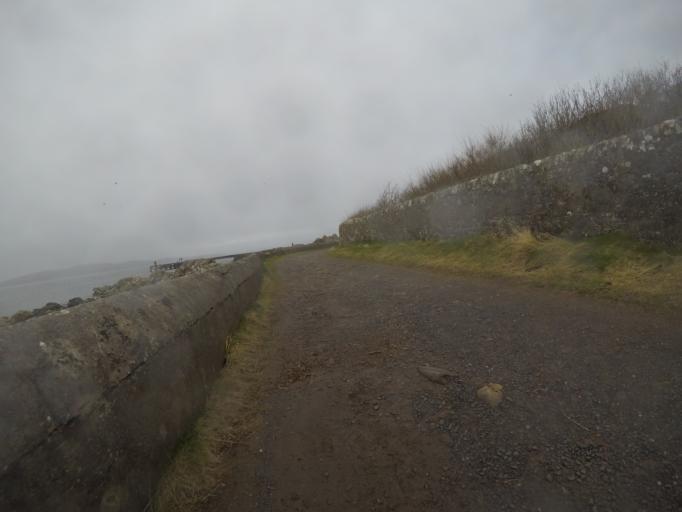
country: GB
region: Scotland
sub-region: North Ayrshire
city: Millport
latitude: 55.7010
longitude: -4.9045
